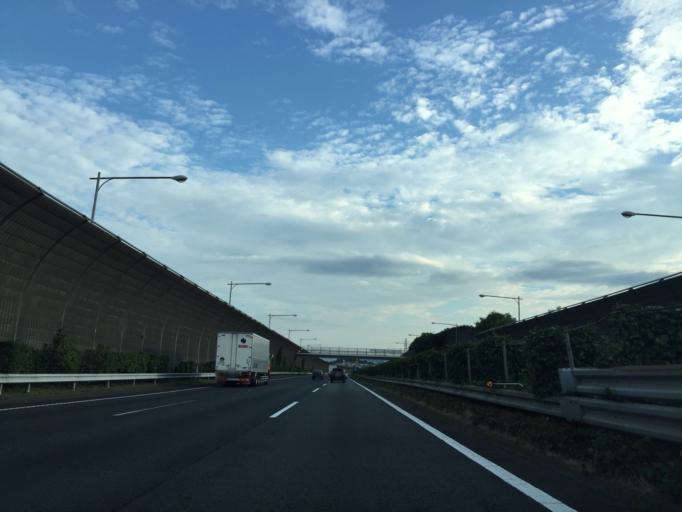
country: JP
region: Kanagawa
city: Isehara
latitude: 35.3968
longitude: 139.2852
